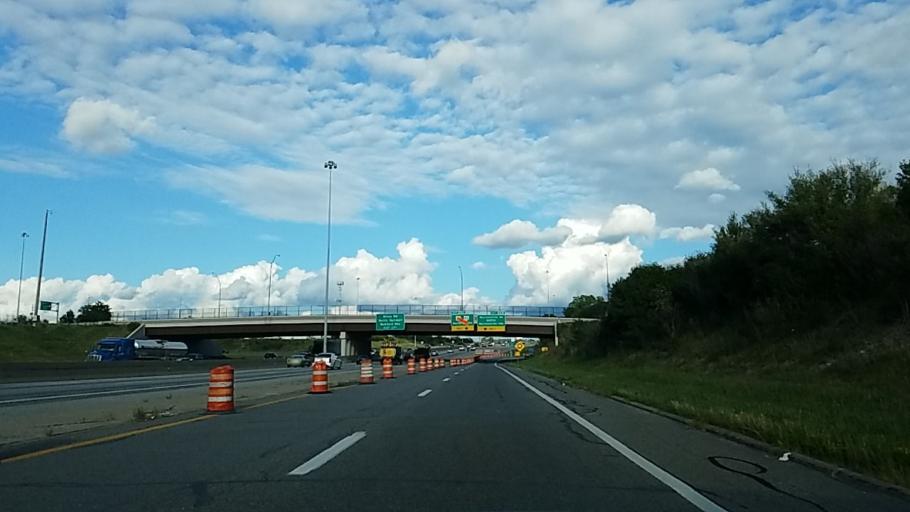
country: US
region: Ohio
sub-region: Cuyahoga County
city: Warrensville Heights
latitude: 41.4246
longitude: -81.5392
